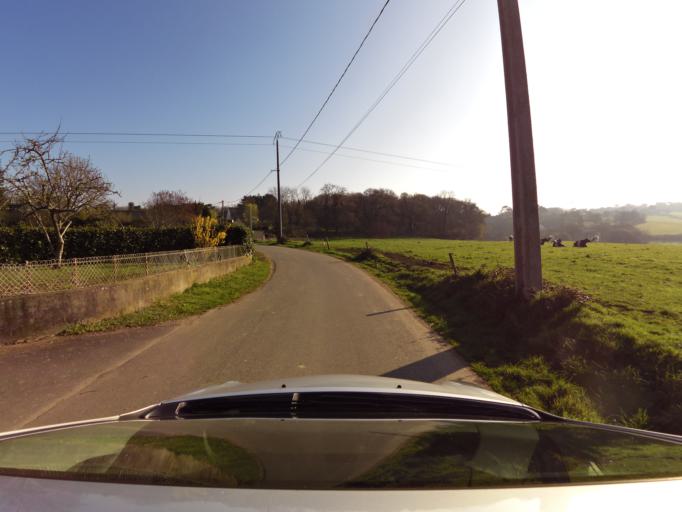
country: FR
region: Brittany
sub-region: Departement du Morbihan
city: Guidel-Plage
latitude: 47.7772
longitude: -3.4932
